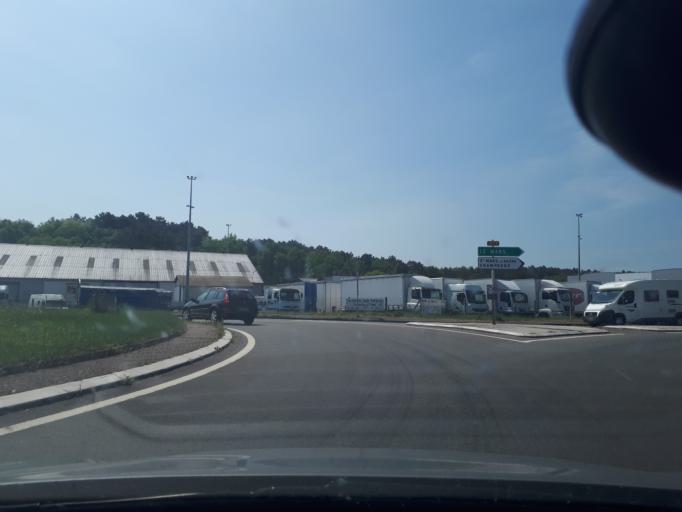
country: FR
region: Pays de la Loire
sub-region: Departement de la Sarthe
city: Montfort-le-Gesnois
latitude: 48.0368
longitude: 0.4266
